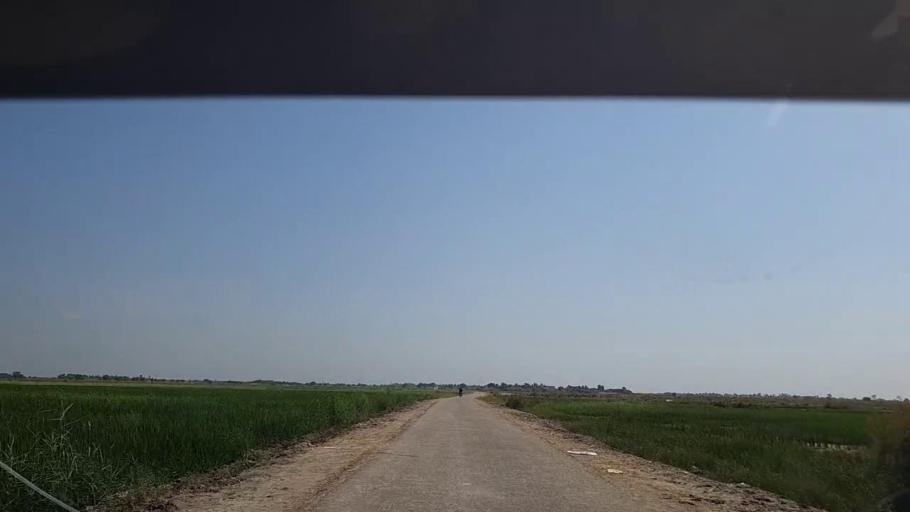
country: PK
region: Sindh
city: Kandhkot
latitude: 28.1788
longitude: 69.1593
